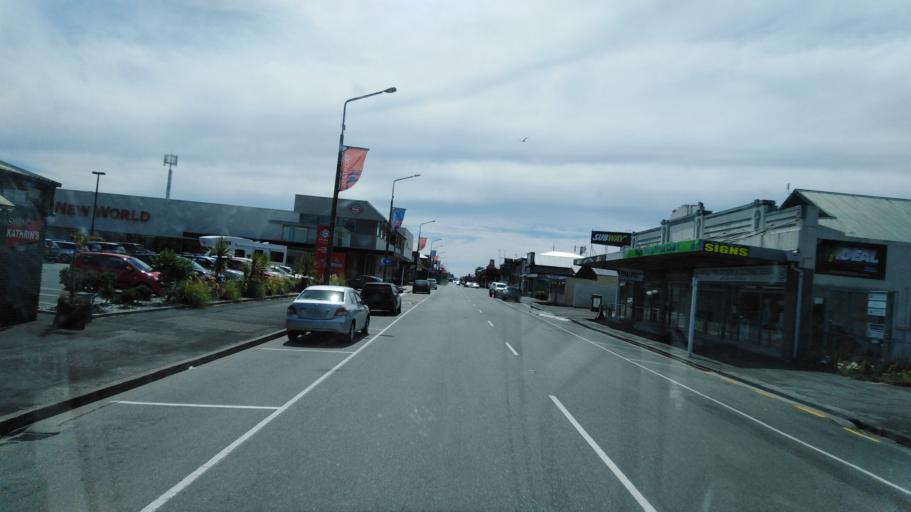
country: NZ
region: West Coast
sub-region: Buller District
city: Westport
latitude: -41.7582
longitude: 171.5993
